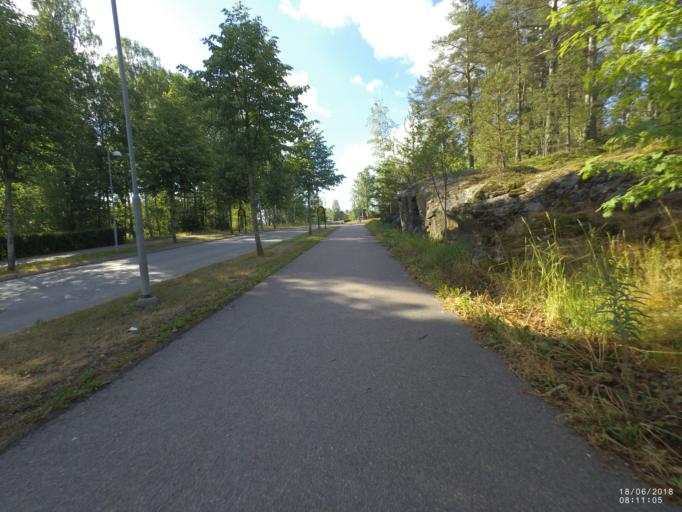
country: SE
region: Soedermanland
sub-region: Nykopings Kommun
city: Nykoping
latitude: 58.7337
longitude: 17.0223
